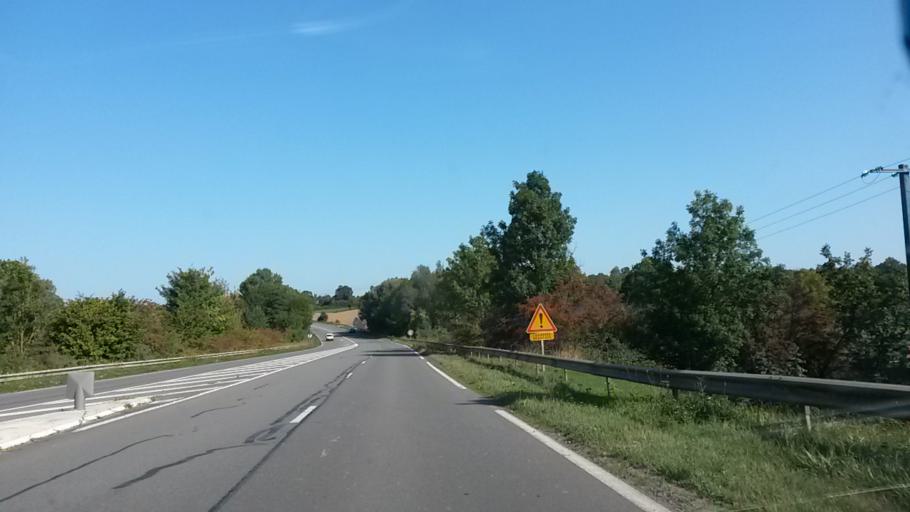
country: FR
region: Nord-Pas-de-Calais
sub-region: Departement du Nord
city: Avesnes-sur-Helpe
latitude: 50.0587
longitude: 3.9331
